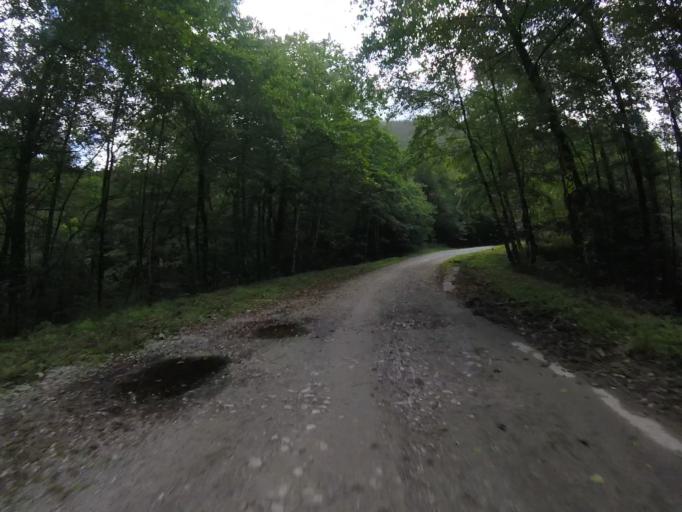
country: ES
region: Basque Country
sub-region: Provincia de Guipuzcoa
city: Elduayen
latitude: 43.1748
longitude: -1.9654
